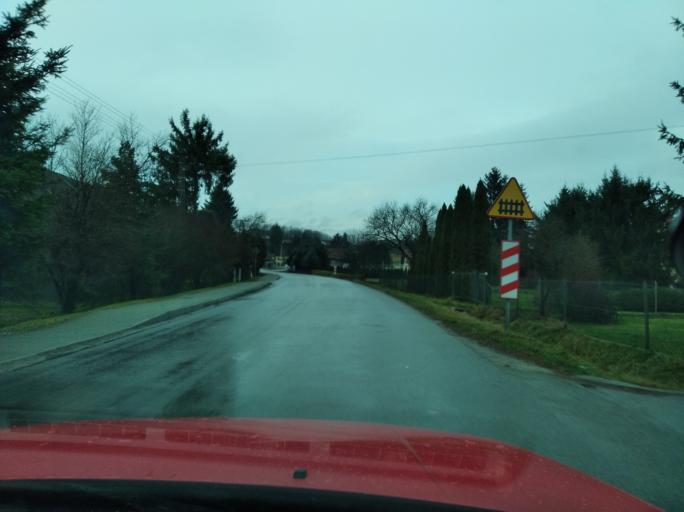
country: PL
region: Subcarpathian Voivodeship
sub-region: Powiat rzeszowski
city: Lutoryz
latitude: 49.9509
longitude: 21.9168
